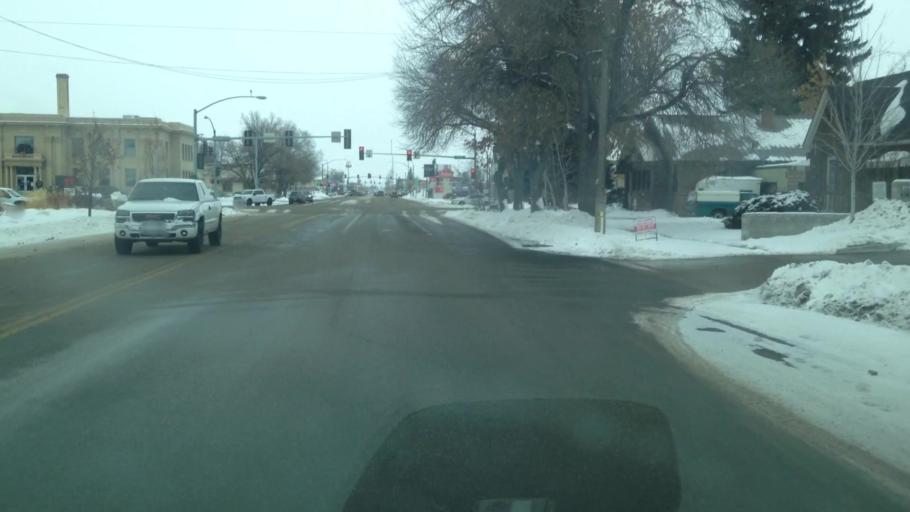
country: US
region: Idaho
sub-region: Madison County
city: Rexburg
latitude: 43.8252
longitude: -111.7781
